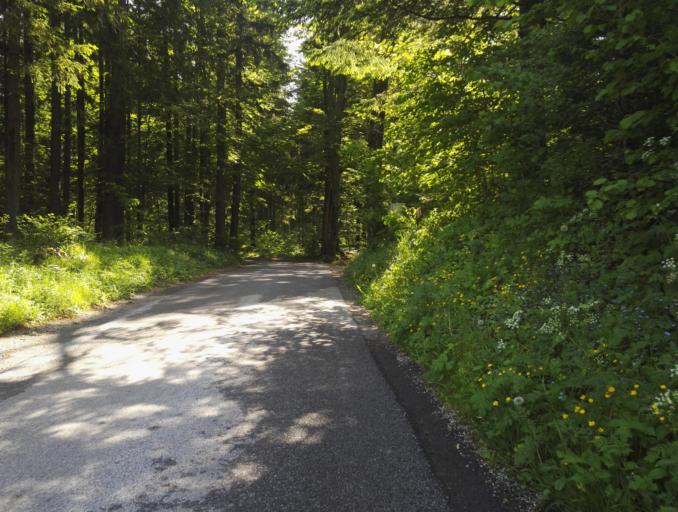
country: AT
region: Styria
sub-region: Politischer Bezirk Graz-Umgebung
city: Stattegg
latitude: 47.1697
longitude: 15.4230
